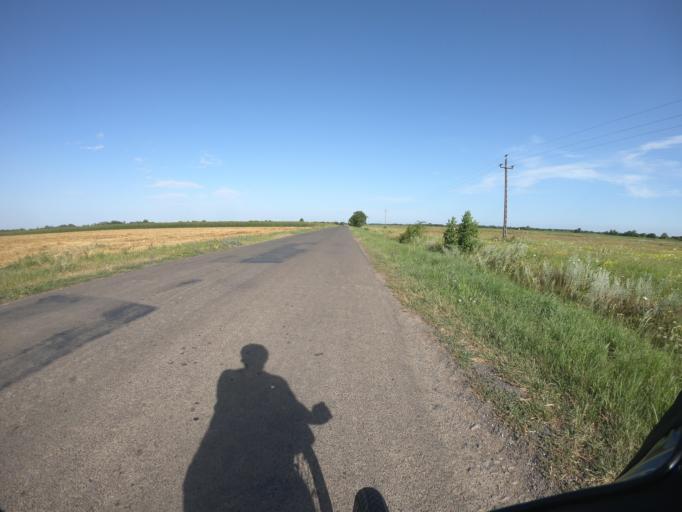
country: HU
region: Hajdu-Bihar
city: Egyek
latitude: 47.6059
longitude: 20.9865
